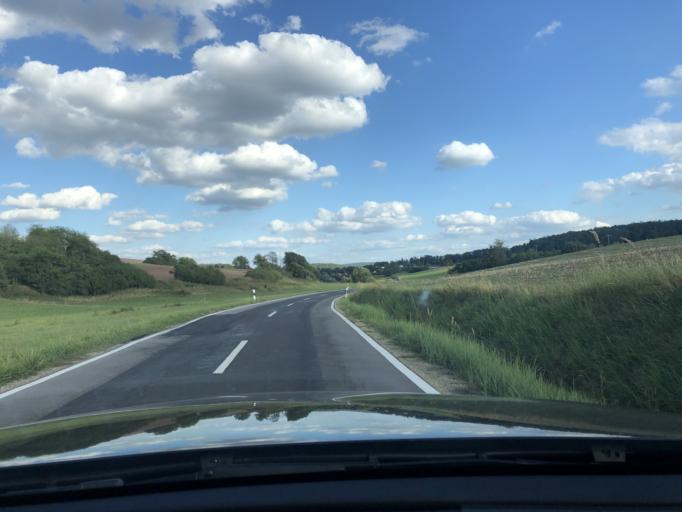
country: DE
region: Bavaria
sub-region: Regierungsbezirk Unterfranken
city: Kirchlauter
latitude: 50.0472
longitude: 10.7027
